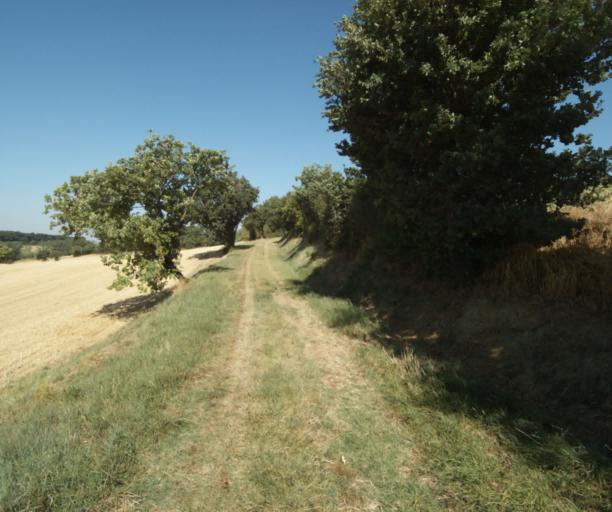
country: FR
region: Midi-Pyrenees
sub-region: Departement de la Haute-Garonne
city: Saint-Felix-Lauragais
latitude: 43.4994
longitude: 1.9360
